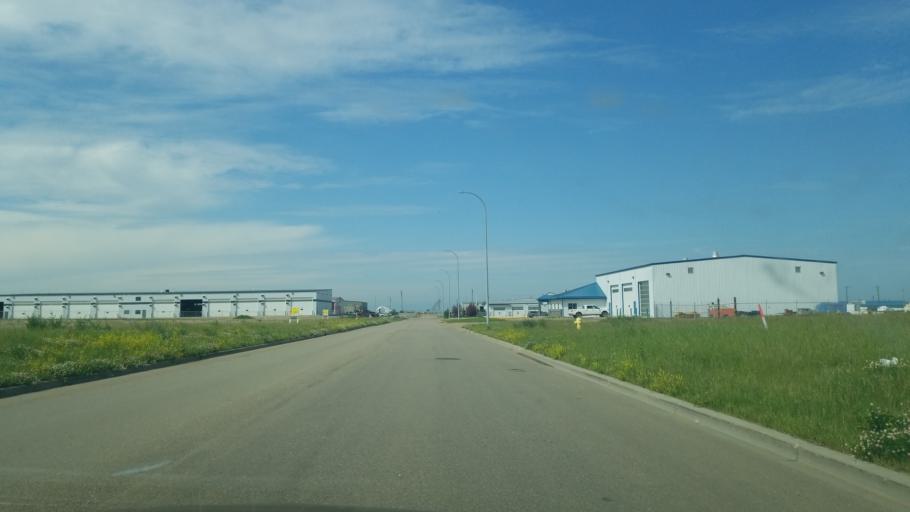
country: CA
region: Saskatchewan
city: Lloydminster
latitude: 53.2883
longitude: -110.0419
